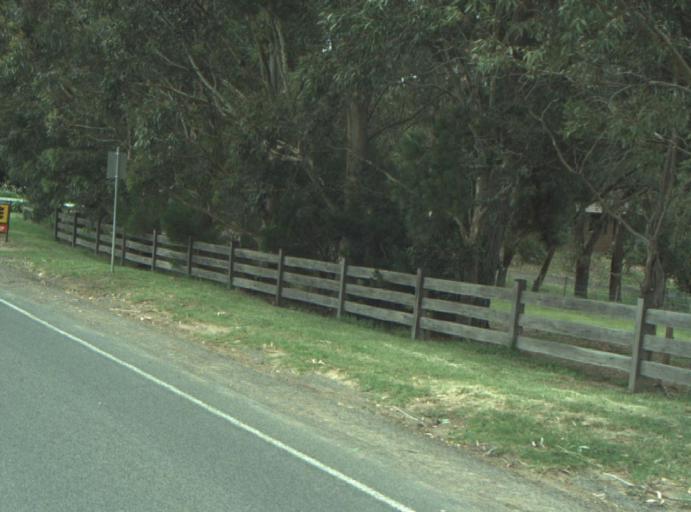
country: AU
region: Victoria
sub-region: Greater Geelong
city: Clifton Springs
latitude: -38.1762
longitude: 144.5517
